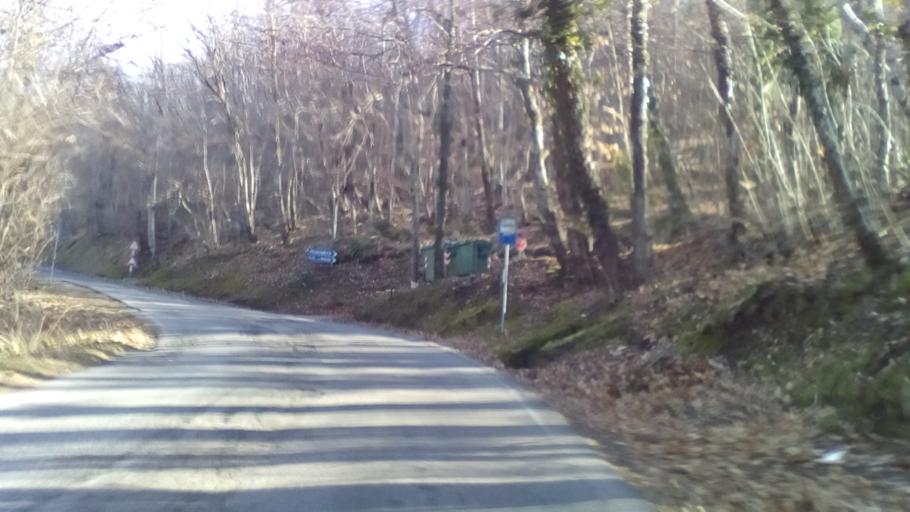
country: IT
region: Tuscany
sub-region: Provincia di Lucca
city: Castiglione di Garfagnana
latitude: 44.1459
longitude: 10.4357
